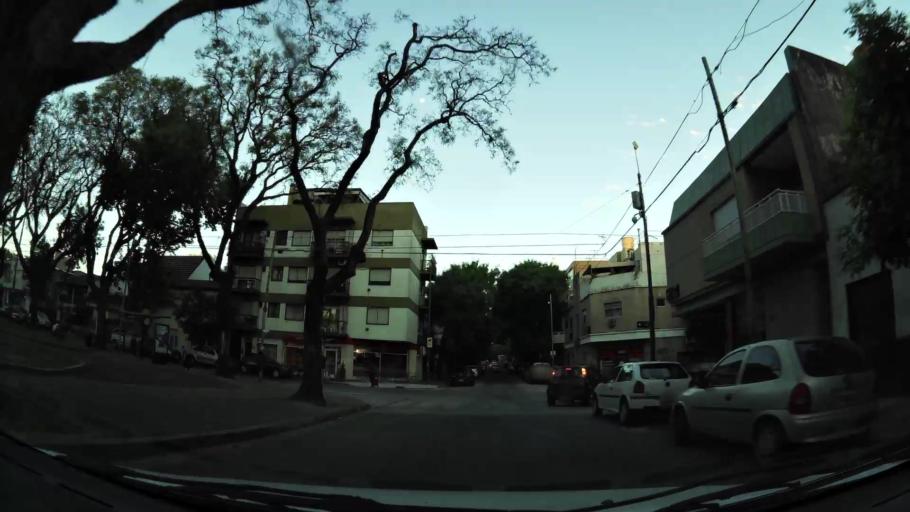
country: AR
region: Buenos Aires
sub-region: Partido de Vicente Lopez
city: Olivos
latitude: -34.5444
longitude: -58.4769
